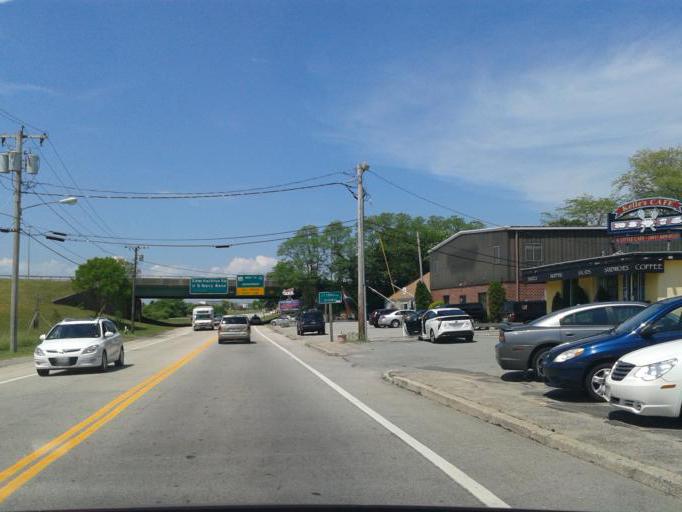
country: US
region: Rhode Island
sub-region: Newport County
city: Newport
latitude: 41.4999
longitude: -71.3172
